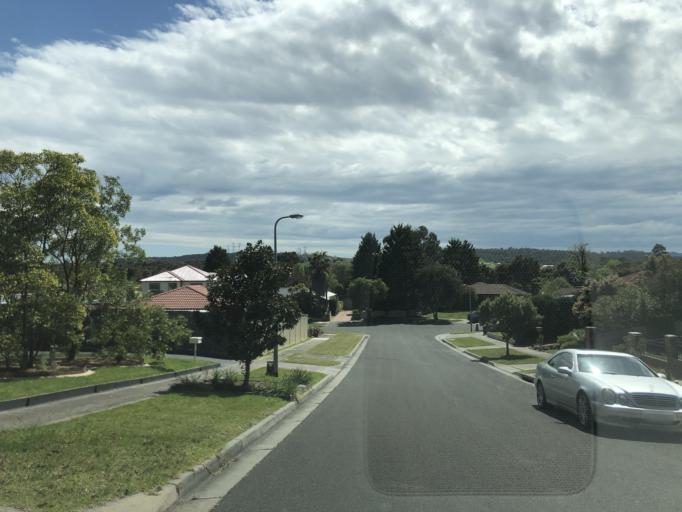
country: AU
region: Victoria
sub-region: Casey
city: Endeavour Hills
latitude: -37.9702
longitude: 145.2602
